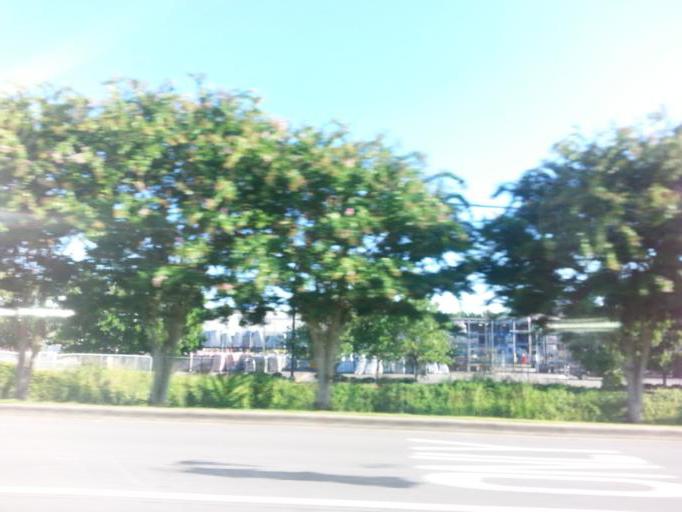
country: US
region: Alabama
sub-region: Lauderdale County
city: East Florence
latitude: 34.8293
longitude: -87.6308
